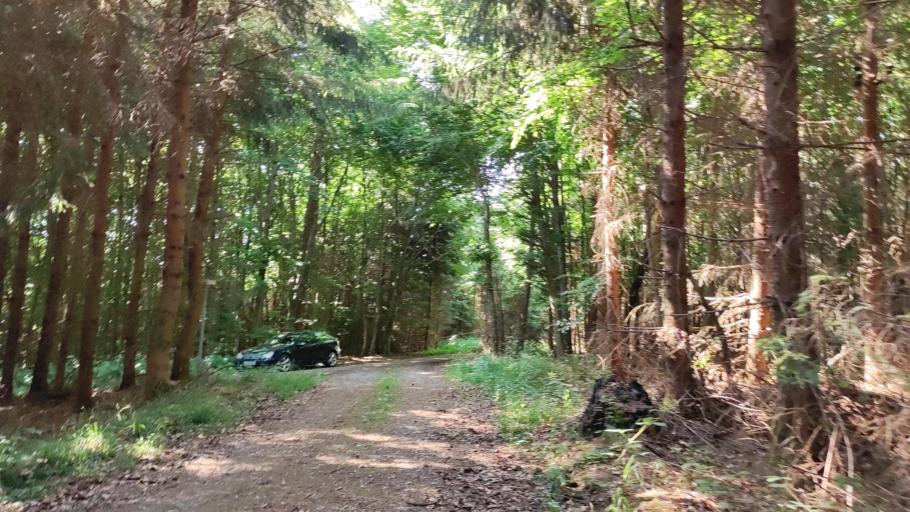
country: DE
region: Bavaria
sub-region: Swabia
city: Dinkelscherben
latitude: 48.3673
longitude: 10.5988
